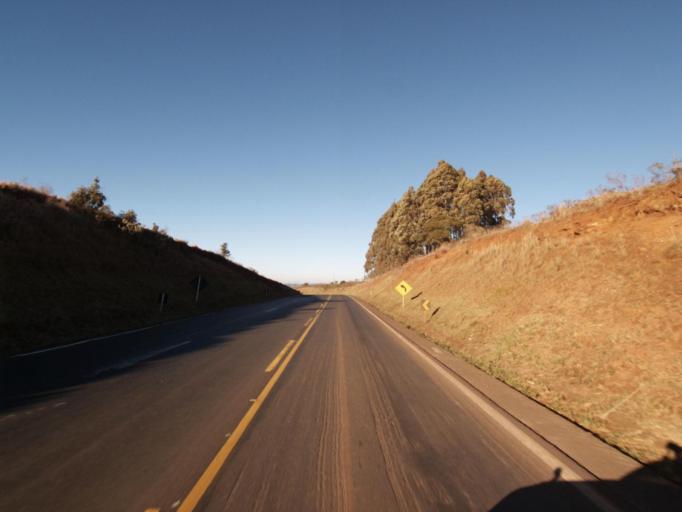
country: AR
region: Misiones
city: Bernardo de Irigoyen
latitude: -26.3189
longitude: -53.5500
